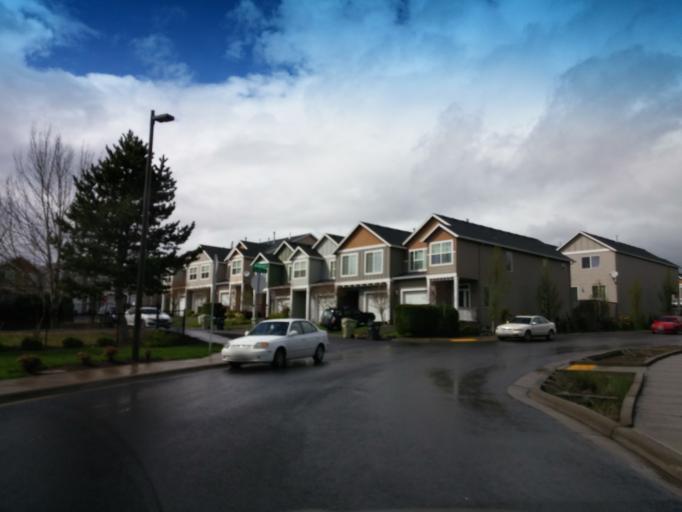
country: US
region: Oregon
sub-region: Washington County
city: Aloha
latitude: 45.5096
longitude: -122.8563
